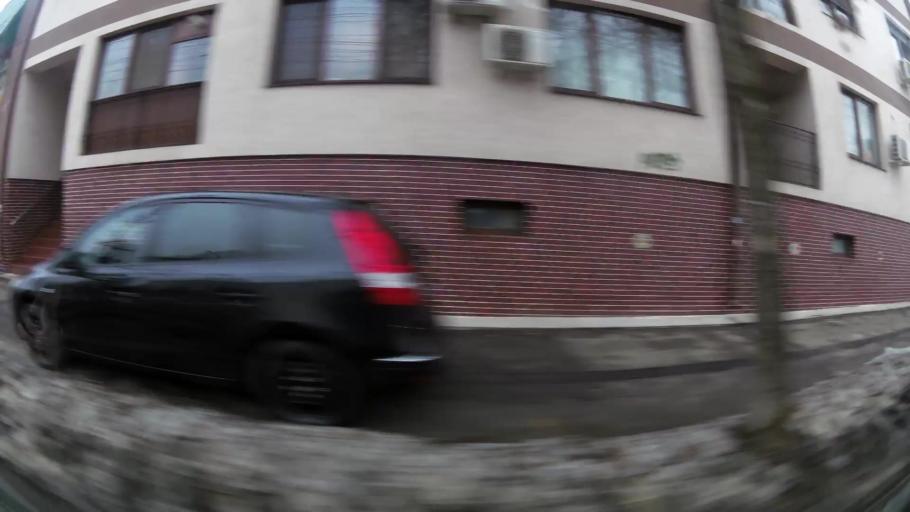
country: RO
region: Bucuresti
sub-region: Municipiul Bucuresti
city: Bucuresti
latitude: 44.4526
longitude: 26.0580
